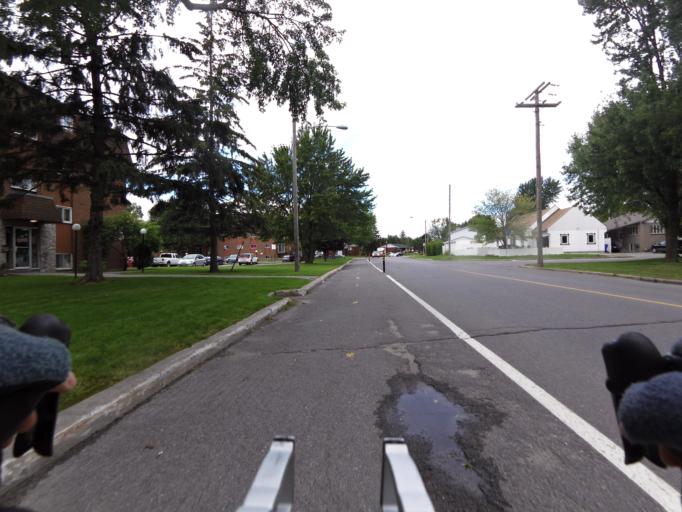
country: CA
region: Quebec
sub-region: Outaouais
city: Gatineau
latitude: 45.4707
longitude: -75.7193
